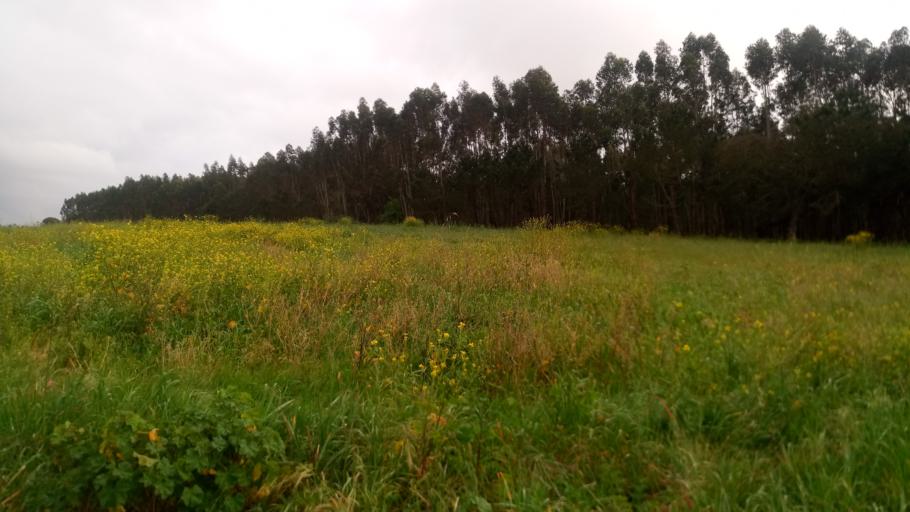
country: PT
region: Leiria
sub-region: Caldas da Rainha
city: Caldas da Rainha
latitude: 39.4351
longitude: -9.1656
